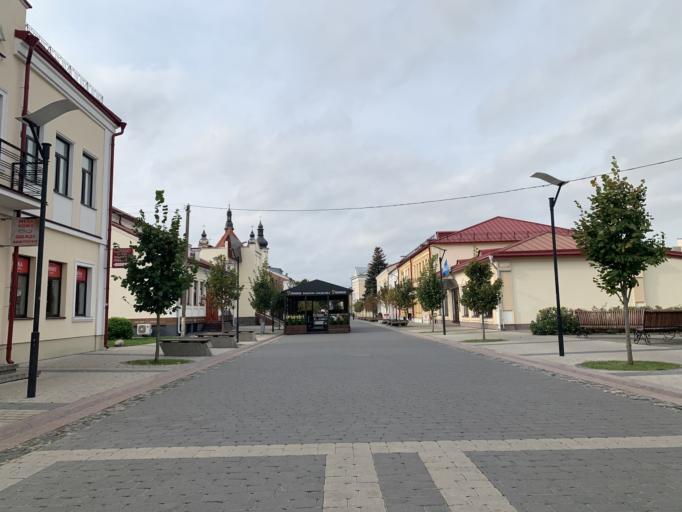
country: BY
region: Brest
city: Pinsk
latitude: 52.1139
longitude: 26.1105
